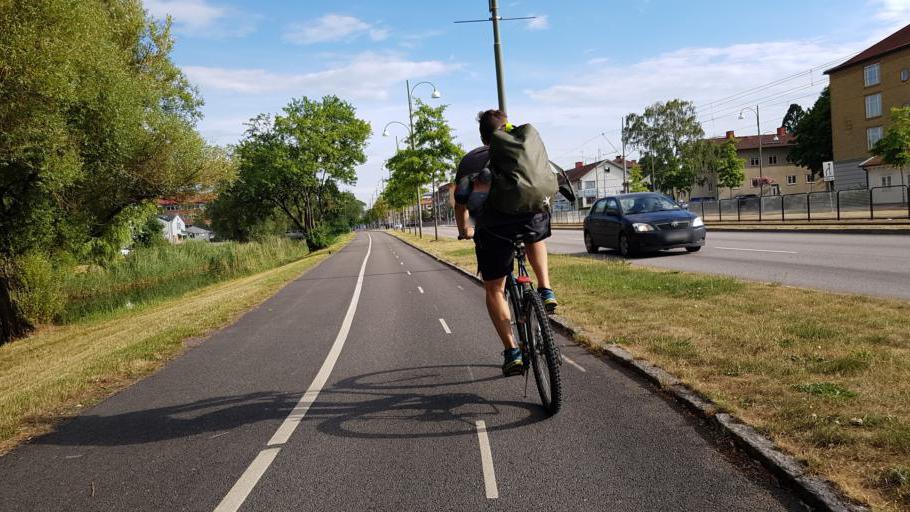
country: SE
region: Vaestra Goetaland
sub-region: Molndal
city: Moelndal
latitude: 57.6612
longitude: 12.0141
